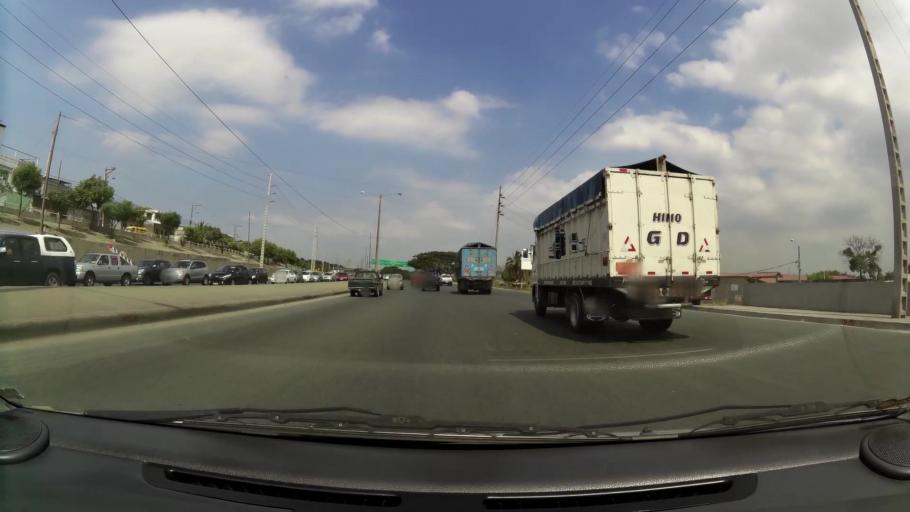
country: EC
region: Guayas
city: Eloy Alfaro
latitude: -2.0695
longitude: -79.9240
